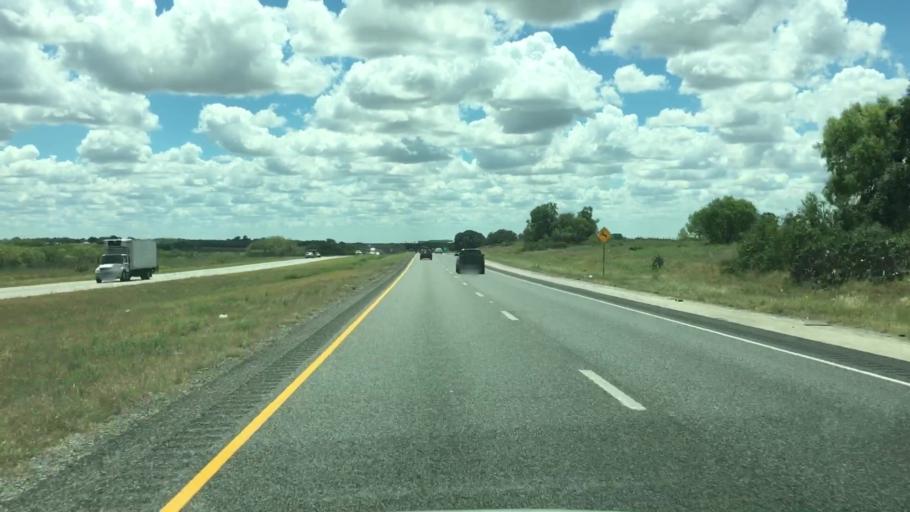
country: US
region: Texas
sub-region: Atascosa County
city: Poteet
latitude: 29.1220
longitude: -98.4313
